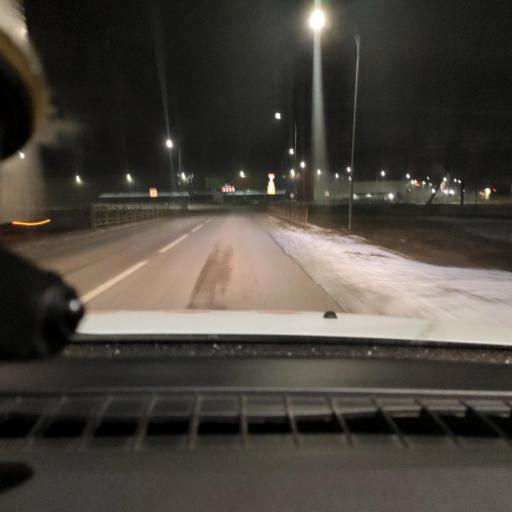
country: RU
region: Samara
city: Samara
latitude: 53.0900
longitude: 50.1355
